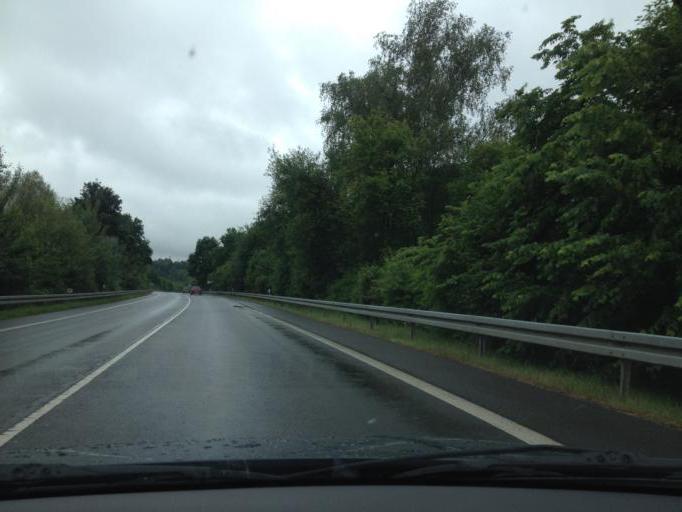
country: DE
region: Saarland
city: Ottweiler
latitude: 49.4201
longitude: 7.1606
